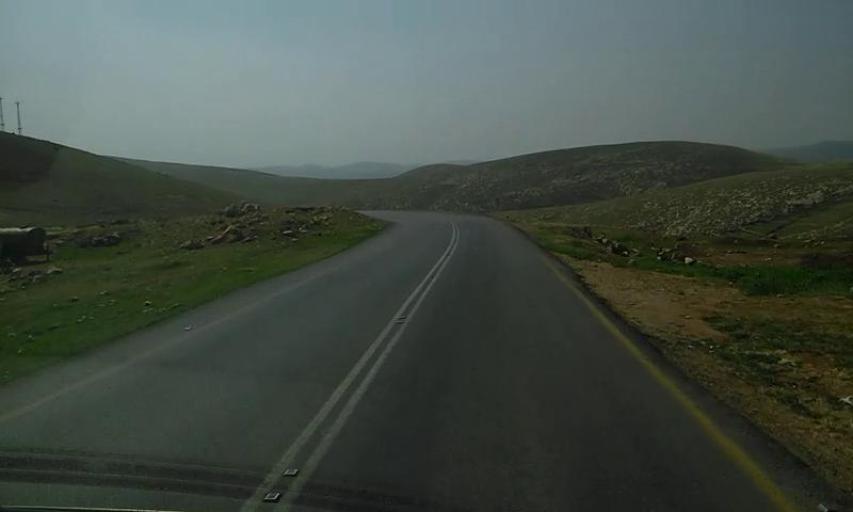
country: PS
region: West Bank
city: Rammun
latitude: 31.9131
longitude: 35.3604
